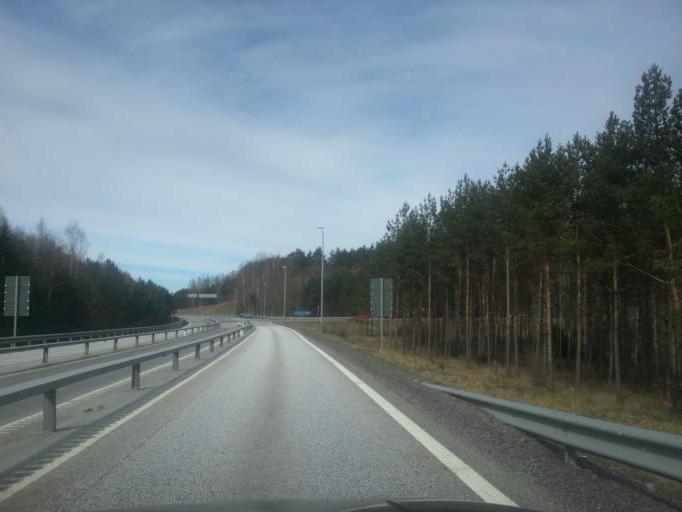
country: SE
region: Joenkoeping
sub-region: Jonkopings Kommun
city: Bankeryd
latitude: 57.8640
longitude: 14.1044
